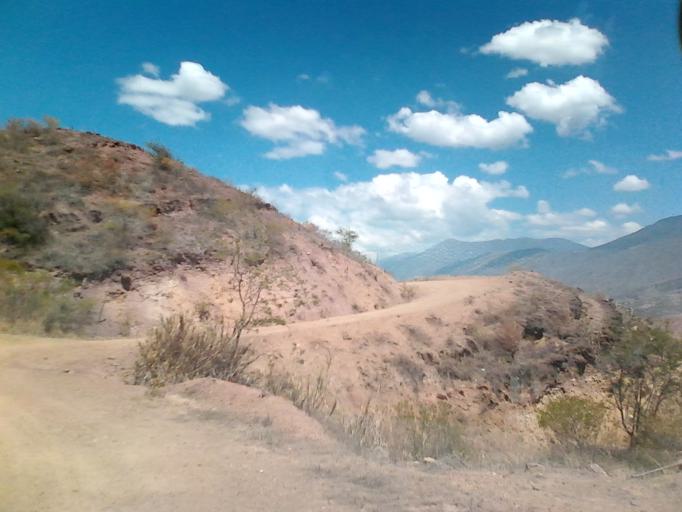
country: CO
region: Boyaca
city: Sachica
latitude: 5.5933
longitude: -73.5721
